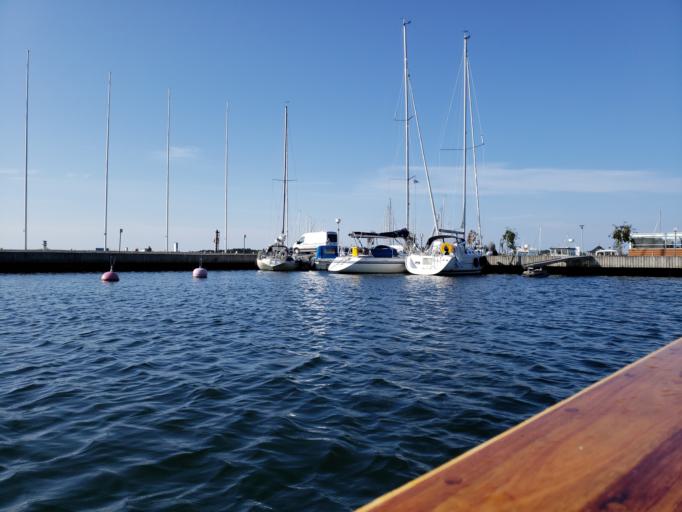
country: FI
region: Varsinais-Suomi
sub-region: Aboland-Turunmaa
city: Dragsfjaerd
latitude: 59.9208
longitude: 22.4102
